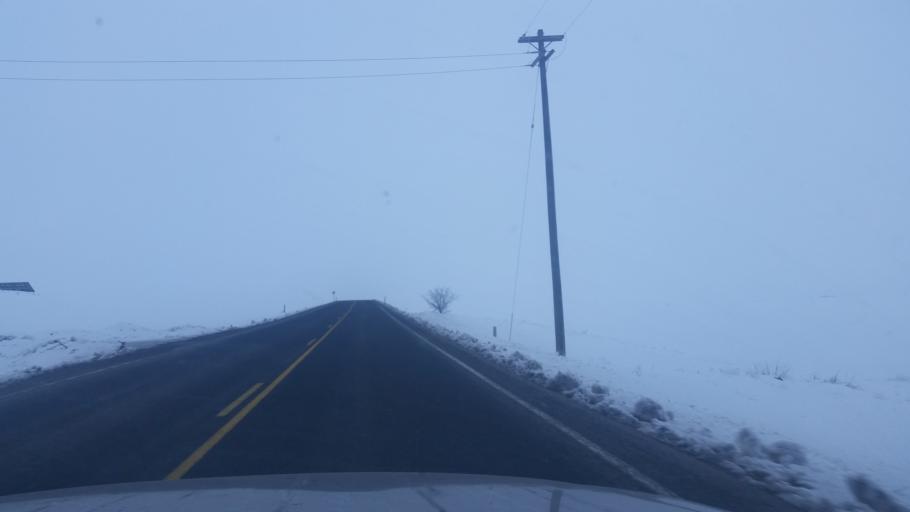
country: US
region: Washington
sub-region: Spokane County
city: Medical Lake
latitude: 47.6513
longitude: -117.8413
